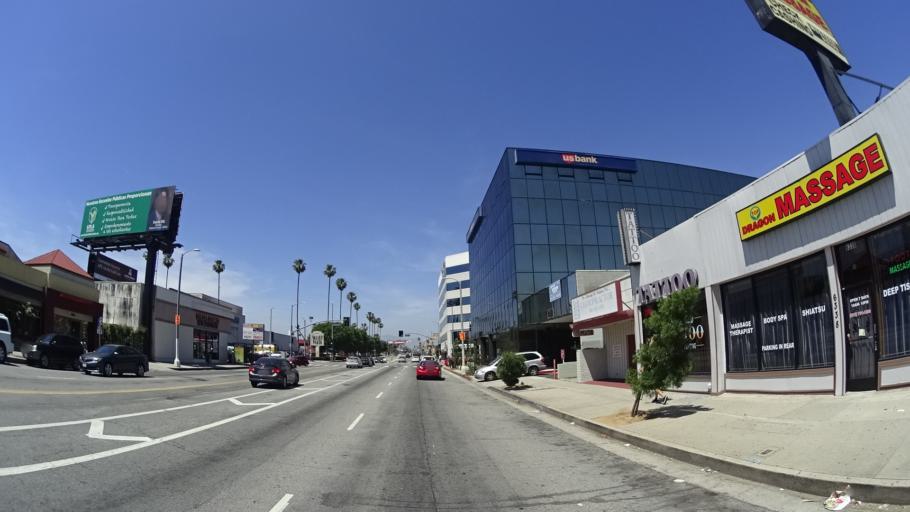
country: US
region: California
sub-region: Los Angeles County
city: North Hollywood
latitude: 34.1859
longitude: -118.3965
